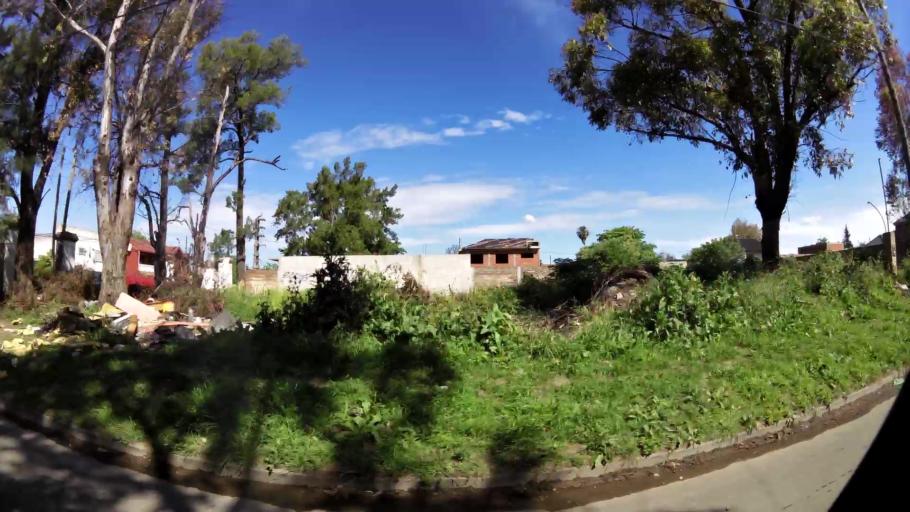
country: AR
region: Buenos Aires
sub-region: Partido de Almirante Brown
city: Adrogue
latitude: -34.7871
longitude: -58.3583
